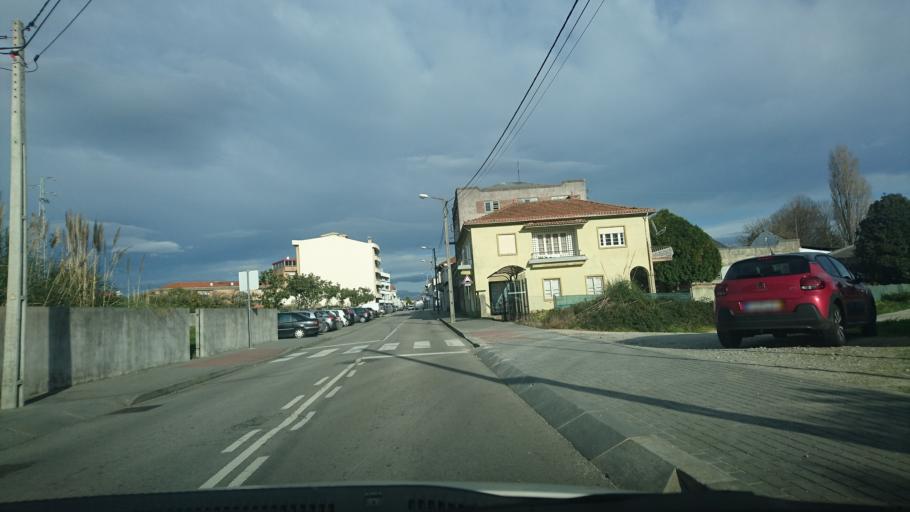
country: PT
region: Aveiro
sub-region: Santa Maria da Feira
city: Pacos de Brandao
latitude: 40.9722
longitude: -8.5846
